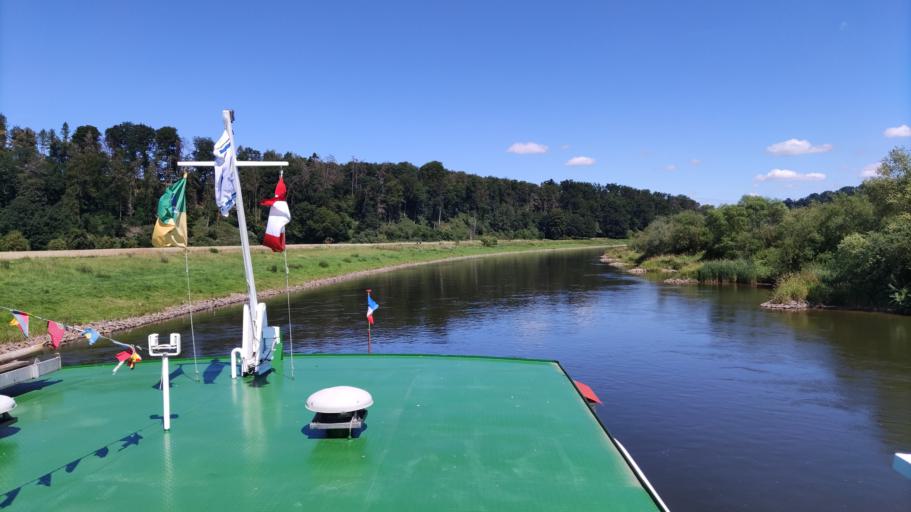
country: DE
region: Lower Saxony
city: Furstenberg
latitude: 51.7196
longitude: 9.3872
